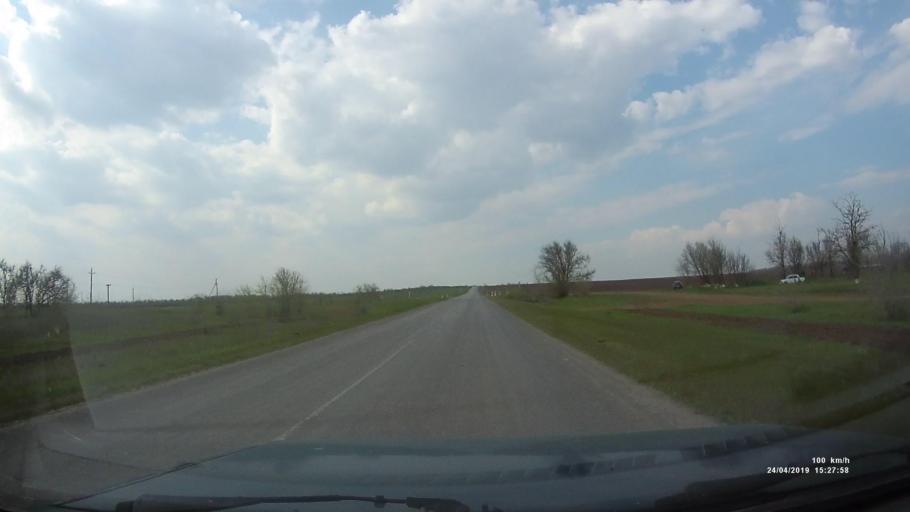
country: RU
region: Rostov
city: Remontnoye
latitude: 46.5723
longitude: 43.0219
